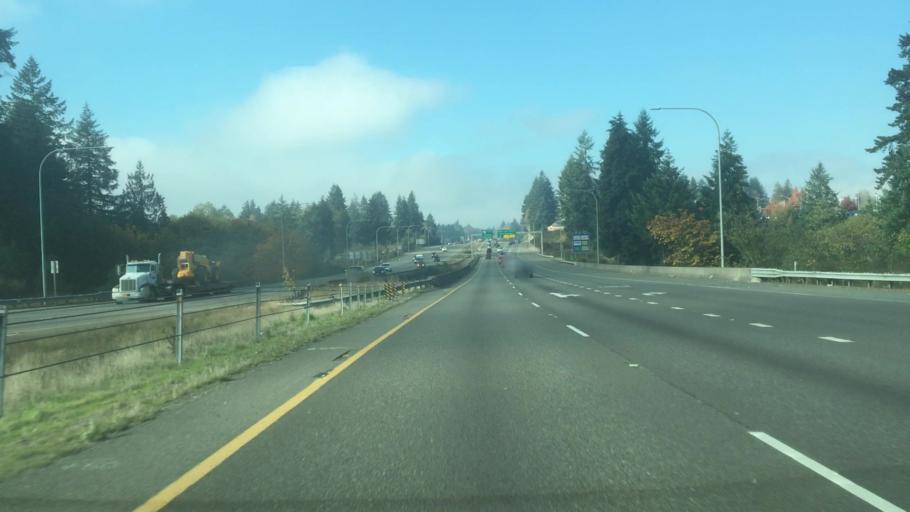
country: US
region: Washington
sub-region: Thurston County
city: Tumwater
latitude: 47.0268
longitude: -122.9294
